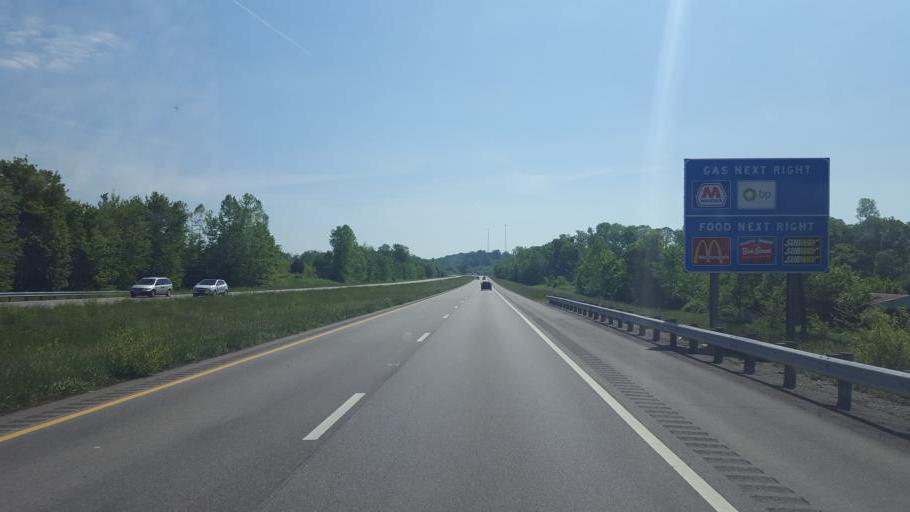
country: US
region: Ohio
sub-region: Jackson County
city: Oak Hill
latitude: 38.8864
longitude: -82.4016
